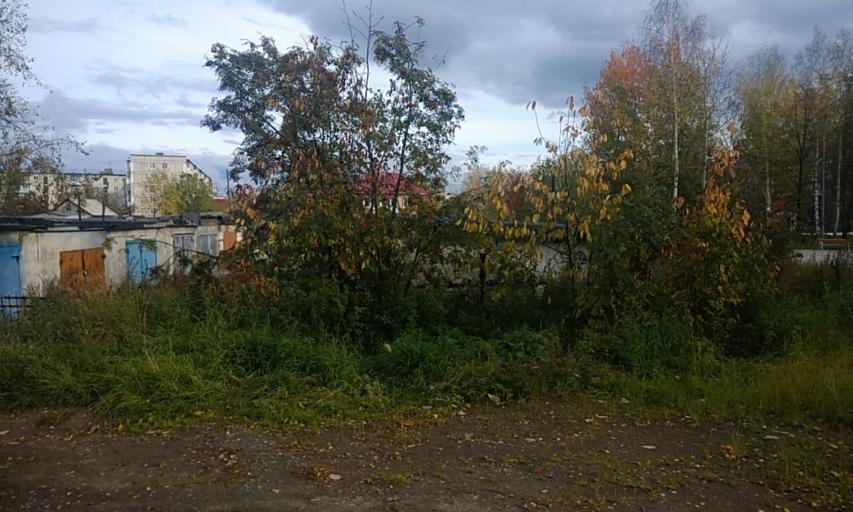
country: RU
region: Sverdlovsk
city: Krasnoural'sk
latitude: 58.3572
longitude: 60.0424
